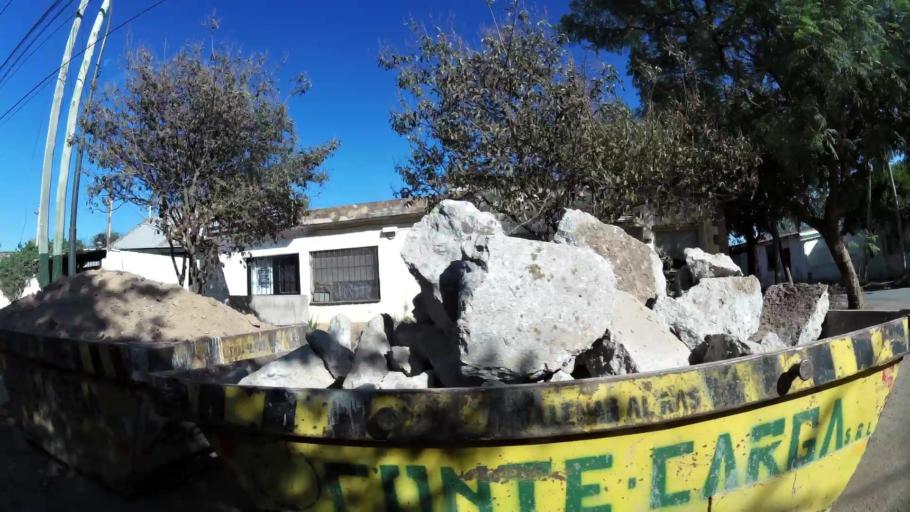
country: AR
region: Cordoba
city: Villa Allende
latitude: -31.3292
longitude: -64.2617
